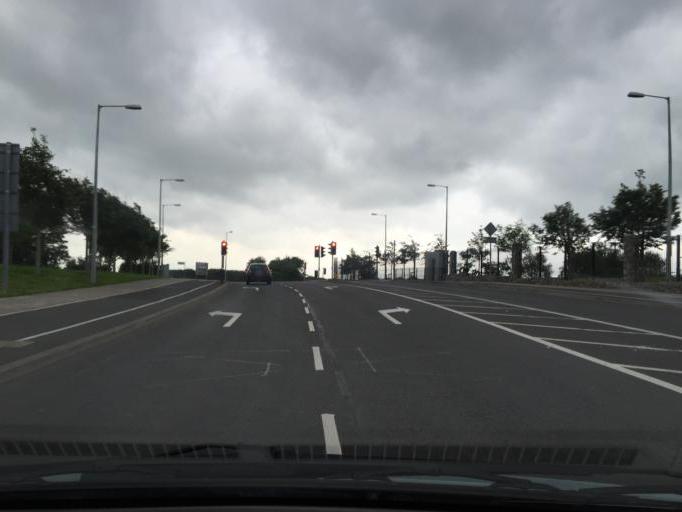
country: IE
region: Connaught
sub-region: Sligo
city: Sligo
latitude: 54.2669
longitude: -8.5032
